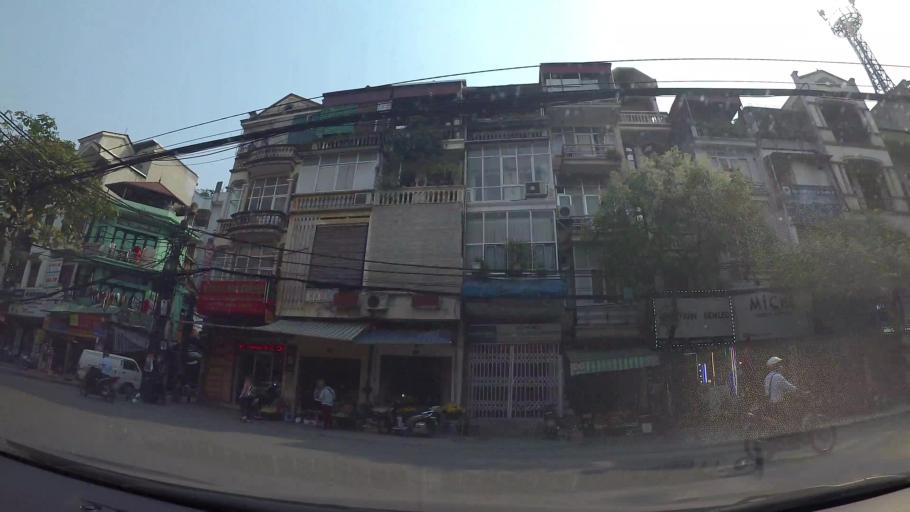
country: VN
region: Ha Noi
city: Thanh Xuan
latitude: 20.9982
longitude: 105.8218
